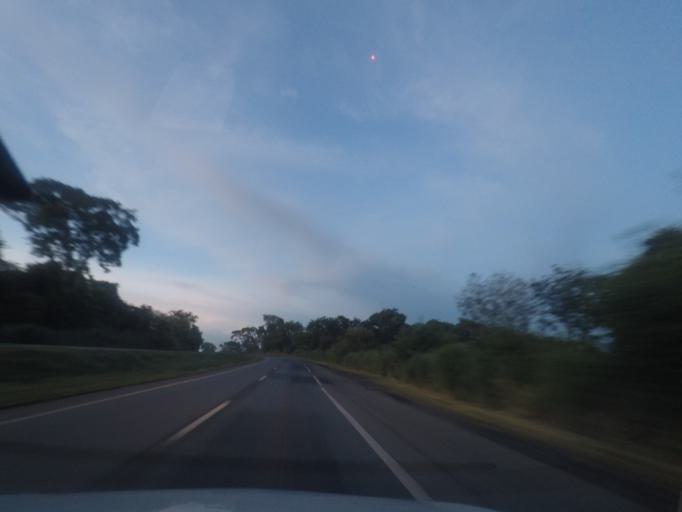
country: BR
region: Goias
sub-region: Pontalina
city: Pontalina
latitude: -17.4857
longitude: -49.2100
